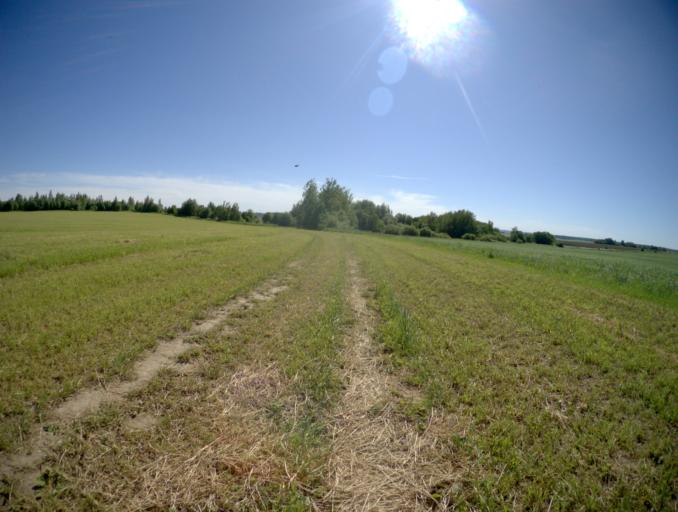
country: RU
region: Vladimir
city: Yur'yev-Pol'skiy
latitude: 56.6104
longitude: 39.8243
